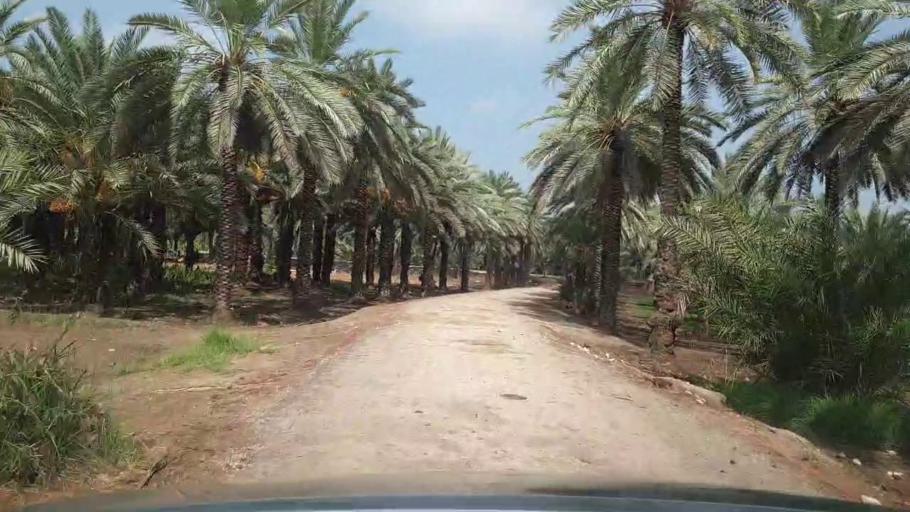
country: PK
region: Sindh
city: Pir jo Goth
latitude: 27.6068
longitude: 68.6894
